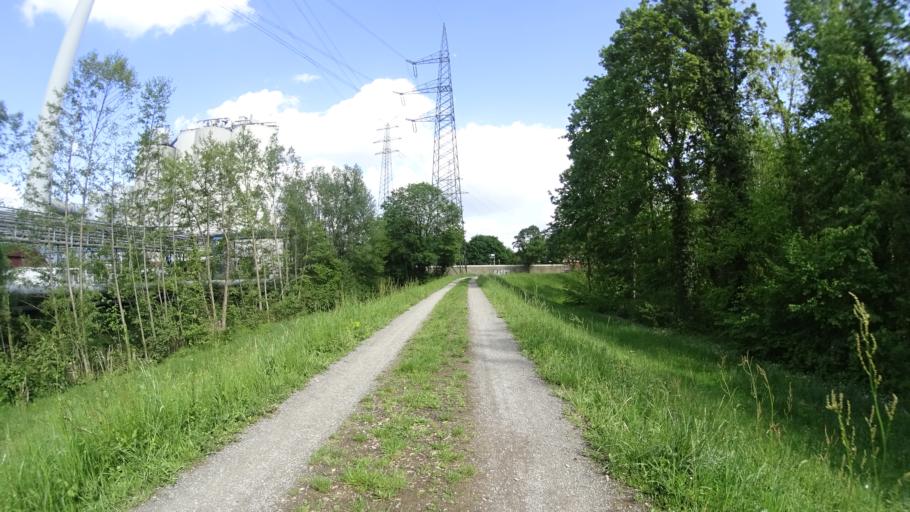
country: DE
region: Baden-Wuerttemberg
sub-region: Karlsruhe Region
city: Rheinstetten
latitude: 49.0109
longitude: 8.3061
